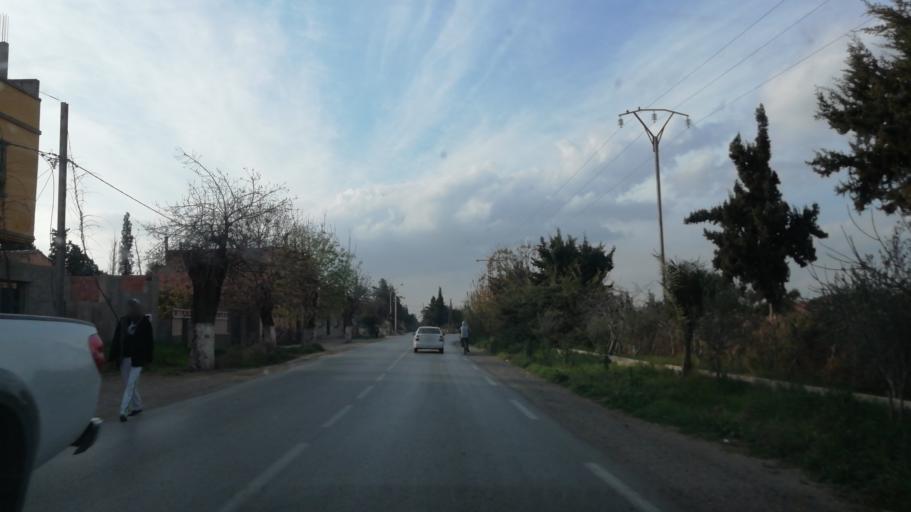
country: DZ
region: Mascara
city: Mascara
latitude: 35.5977
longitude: 0.0554
